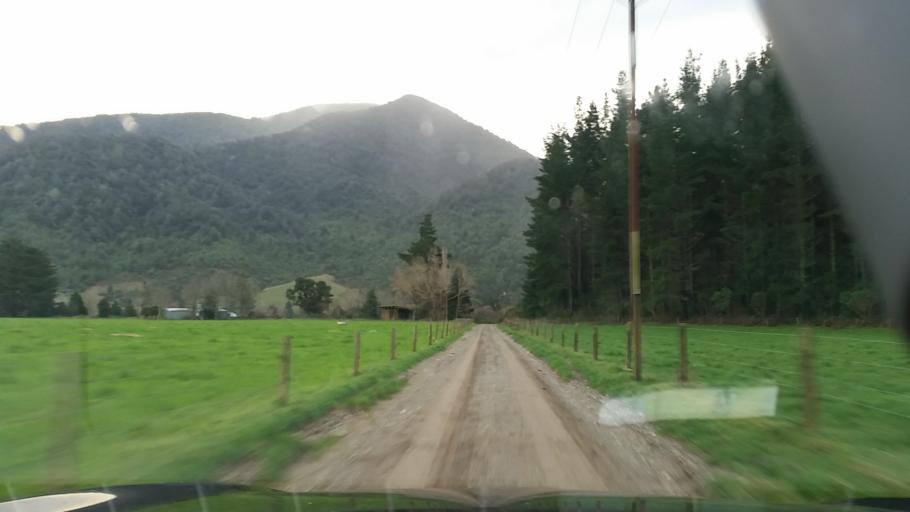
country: NZ
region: Marlborough
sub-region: Marlborough District
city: Picton
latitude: -41.2071
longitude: 173.6907
